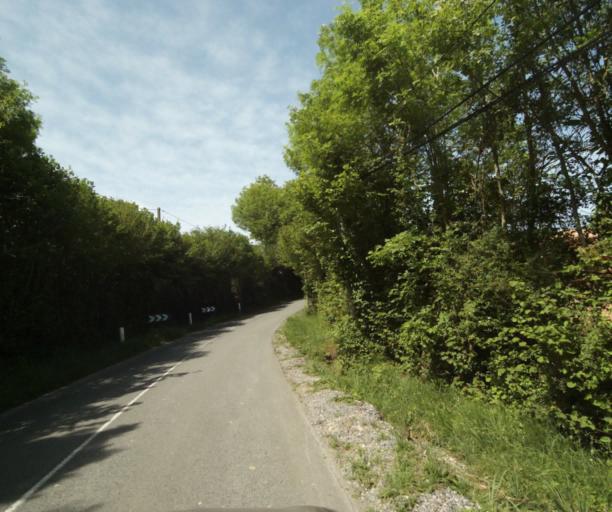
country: FR
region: Aquitaine
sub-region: Departement des Pyrenees-Atlantiques
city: Mouguerre
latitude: 43.4559
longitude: -1.4319
